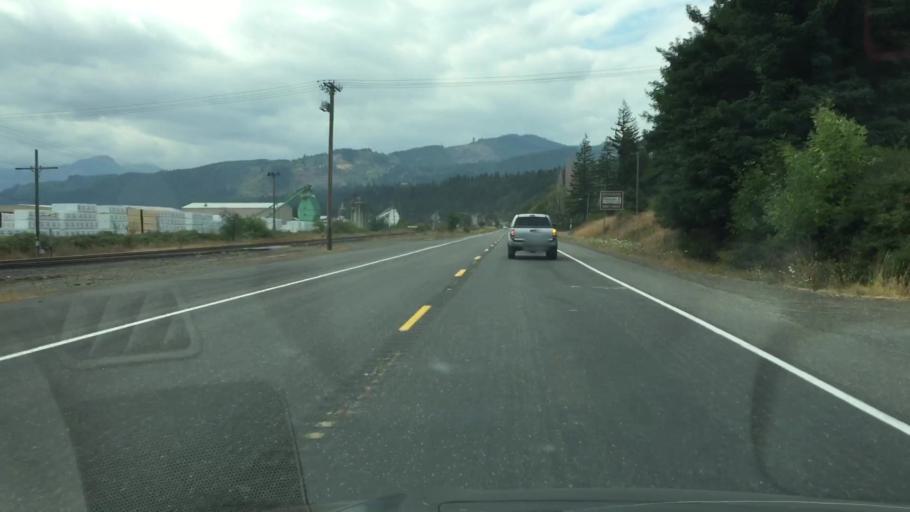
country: US
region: Washington
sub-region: Skamania County
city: Carson
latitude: 45.7119
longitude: -121.7794
